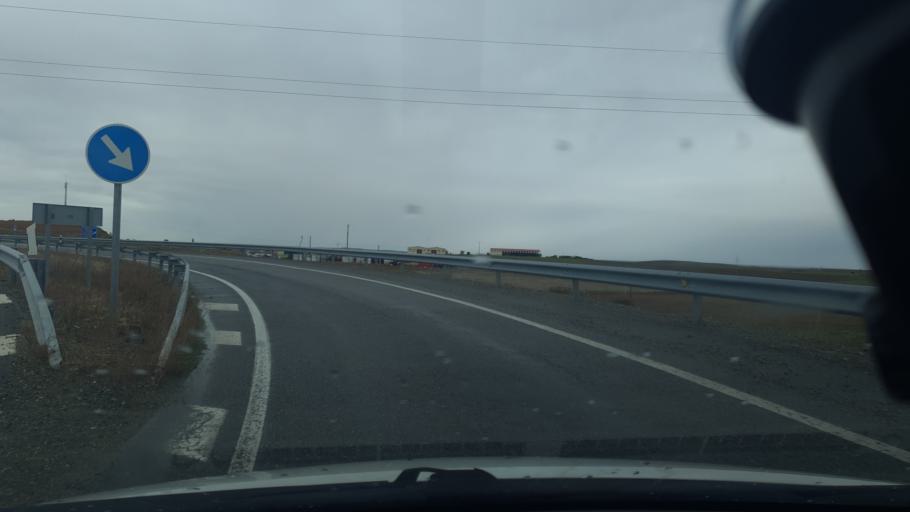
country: ES
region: Castille and Leon
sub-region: Provincia de Segovia
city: Encinillas
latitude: 40.9922
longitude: -4.1405
